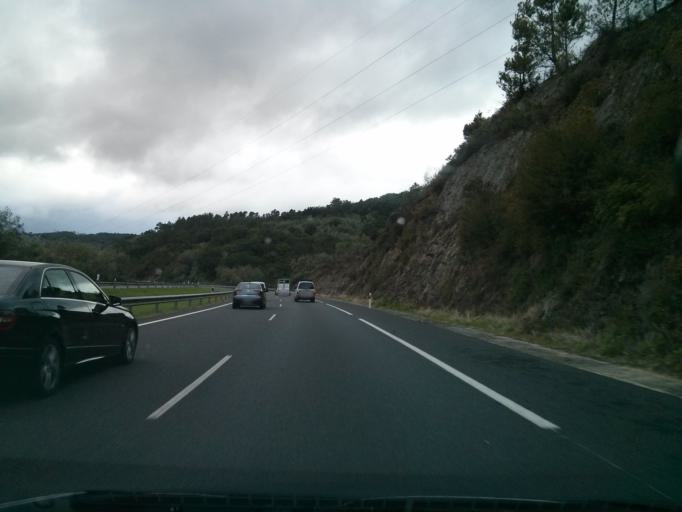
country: ES
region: Galicia
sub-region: Provincia de Ourense
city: Cenlle
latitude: 42.3362
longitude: -8.0504
